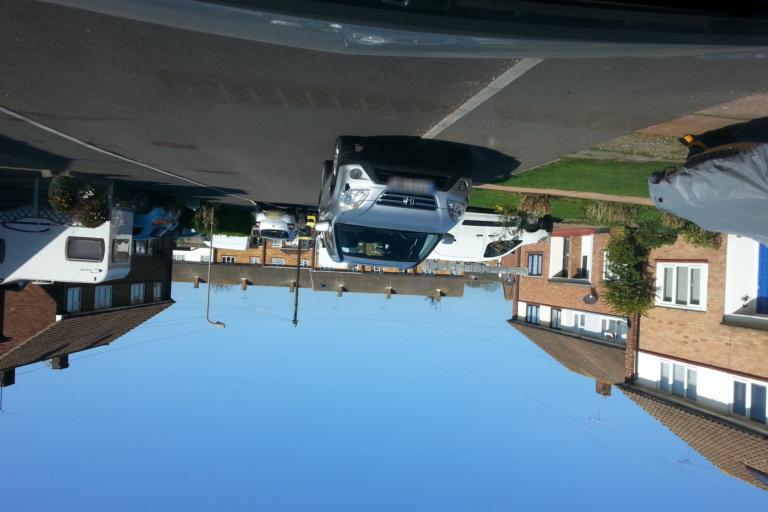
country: GB
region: England
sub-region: Essex
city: Hadleigh
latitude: 51.5607
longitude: 0.5985
